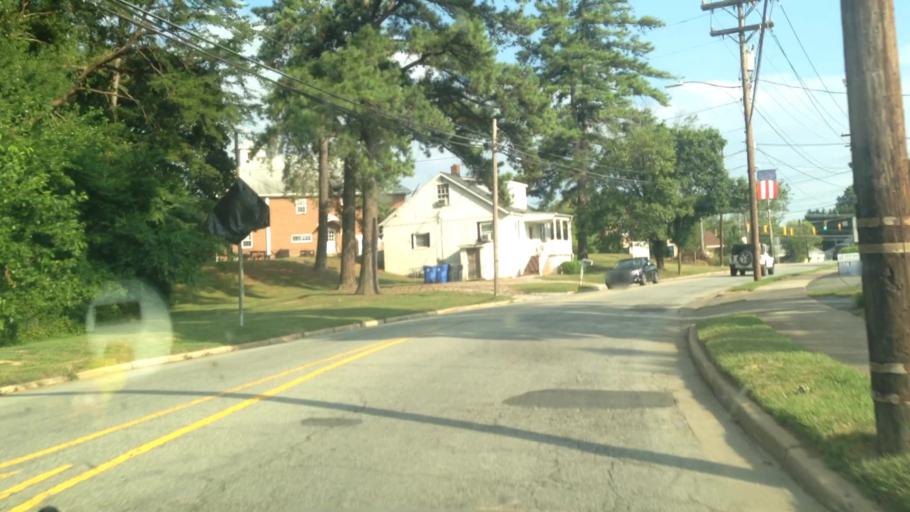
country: US
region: North Carolina
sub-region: Forsyth County
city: Kernersville
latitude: 36.1217
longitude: -80.0752
